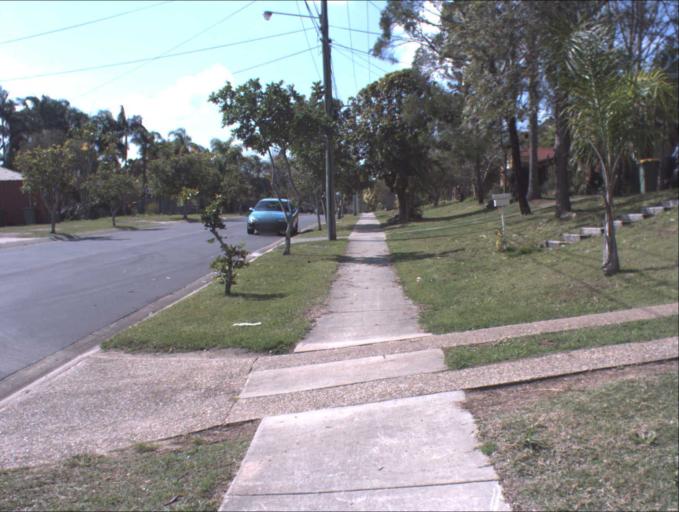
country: AU
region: Queensland
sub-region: Brisbane
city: Sunnybank Hills
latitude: -27.6659
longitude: 153.0533
